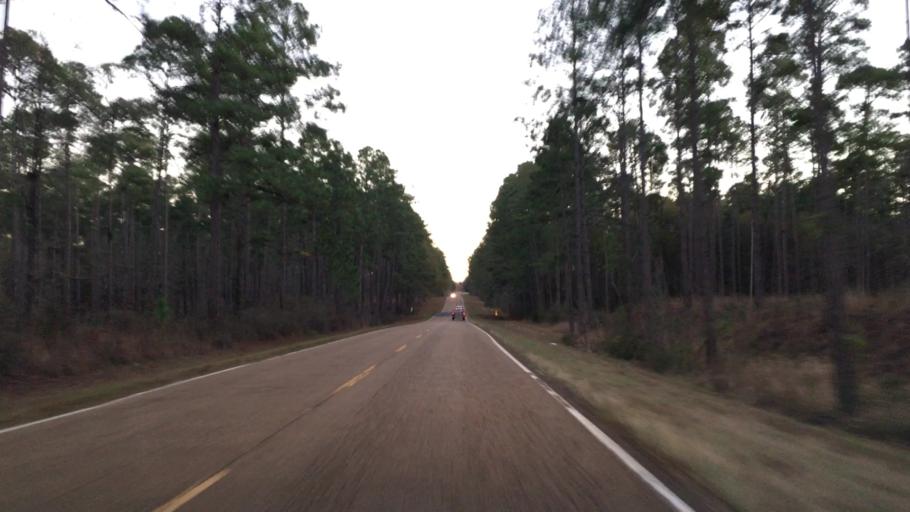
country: US
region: Louisiana
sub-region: Vernon Parish
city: Fort Polk South
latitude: 31.0110
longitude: -93.1862
